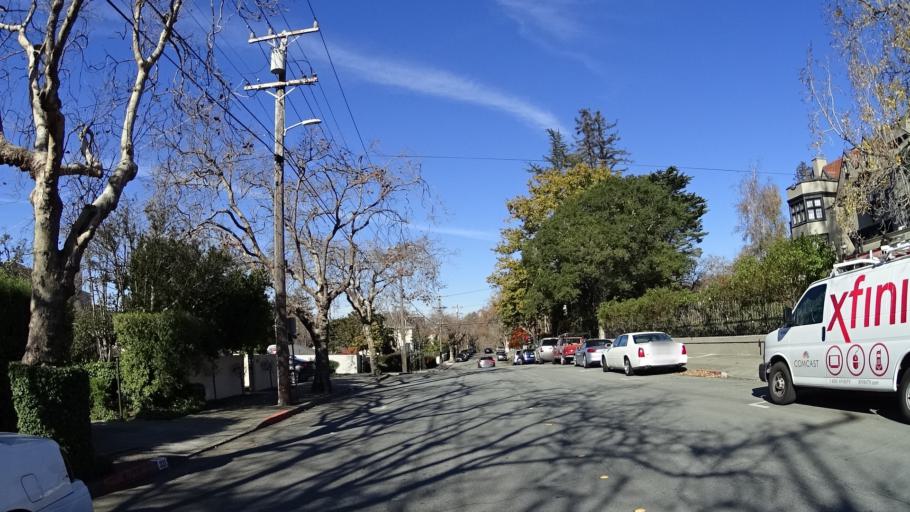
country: US
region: California
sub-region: Alameda County
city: Piedmont
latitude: 37.8247
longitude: -122.2353
